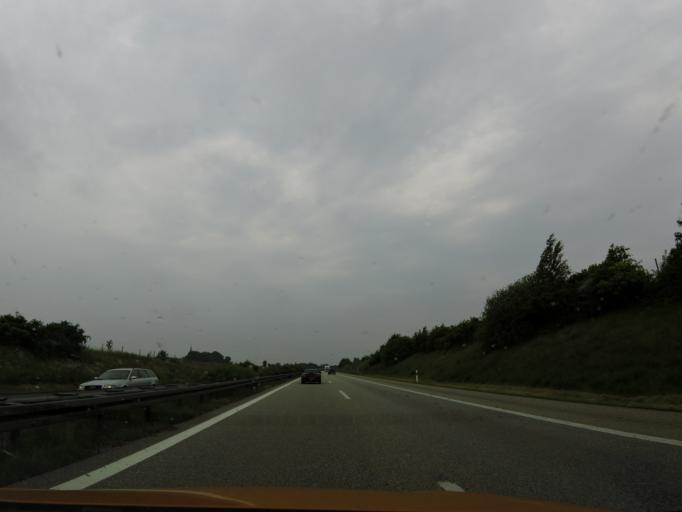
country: DE
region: Mecklenburg-Vorpommern
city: Rehna
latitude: 53.8307
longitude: 11.0163
